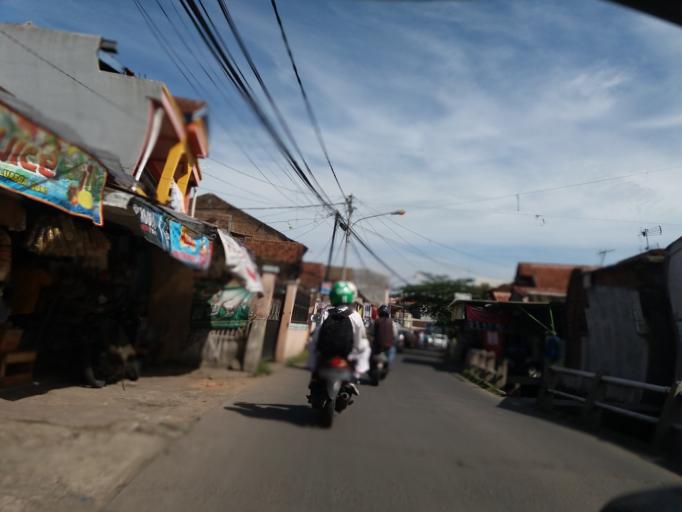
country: ID
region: West Java
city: Margahayukencana
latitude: -6.9456
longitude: 107.6023
